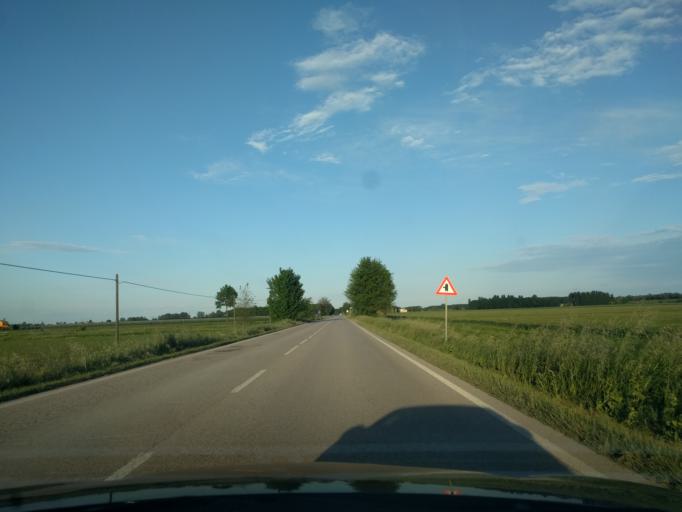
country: IT
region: Veneto
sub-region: Provincia di Rovigo
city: Guarda Veneta
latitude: 44.9832
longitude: 11.8252
